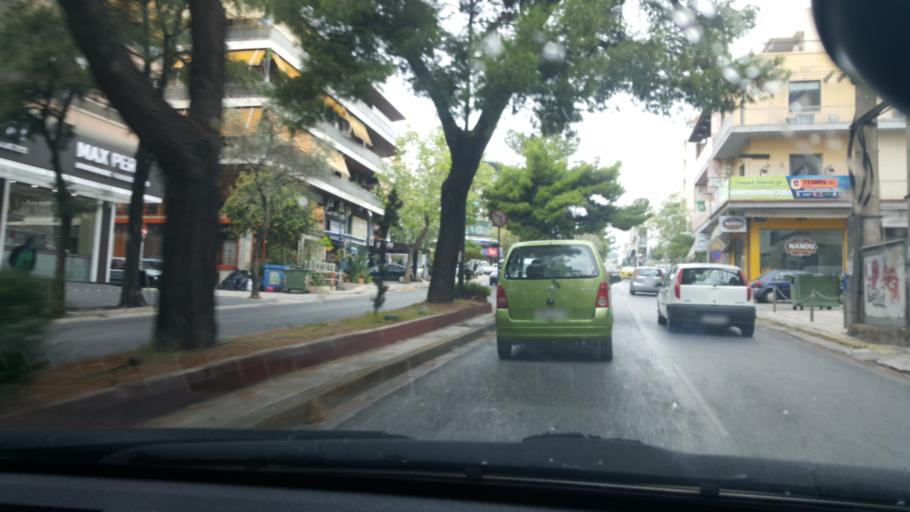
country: GR
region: Attica
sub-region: Nomarchia Athinas
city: Neo Psychiko
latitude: 37.9945
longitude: 23.7742
